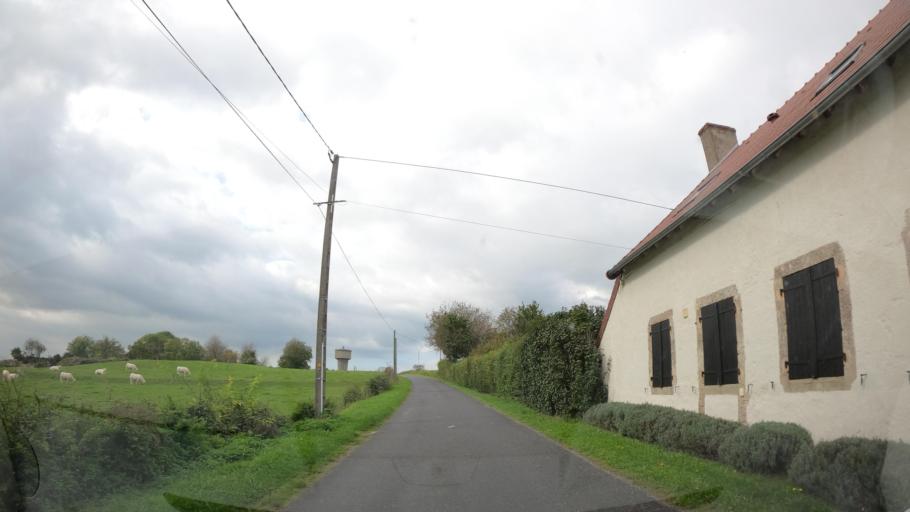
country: FR
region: Auvergne
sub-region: Departement de l'Allier
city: Lapalisse
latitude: 46.3511
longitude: 3.6235
